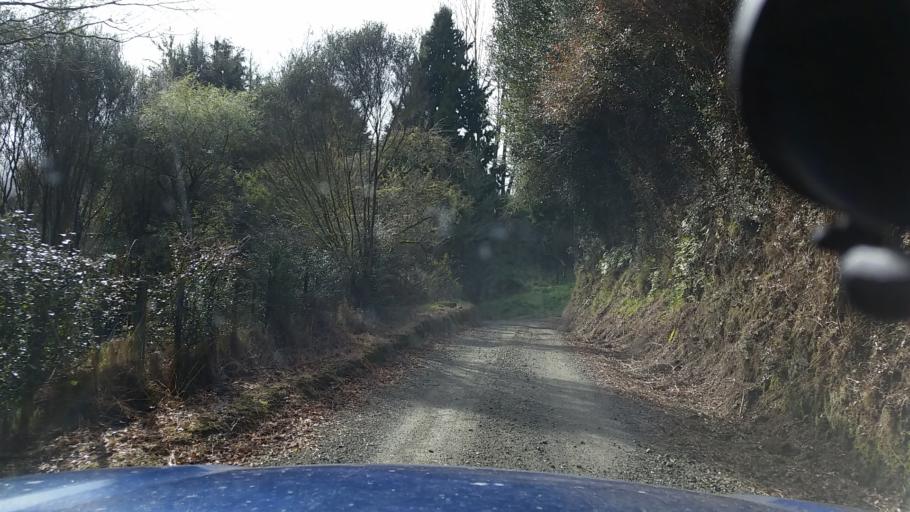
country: NZ
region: Taranaki
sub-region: New Plymouth District
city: Waitara
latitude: -39.0324
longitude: 174.8011
